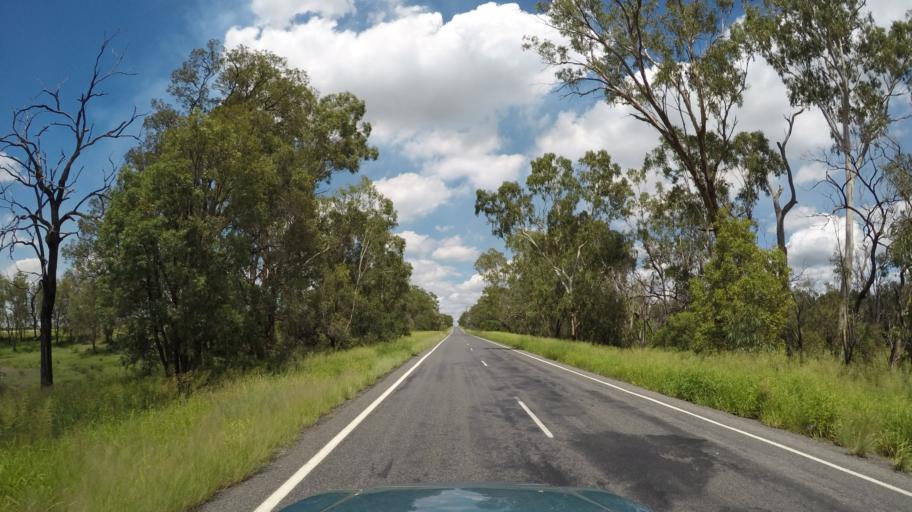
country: AU
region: Queensland
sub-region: Toowoomba
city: Oakey
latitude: -27.9367
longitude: 151.1652
